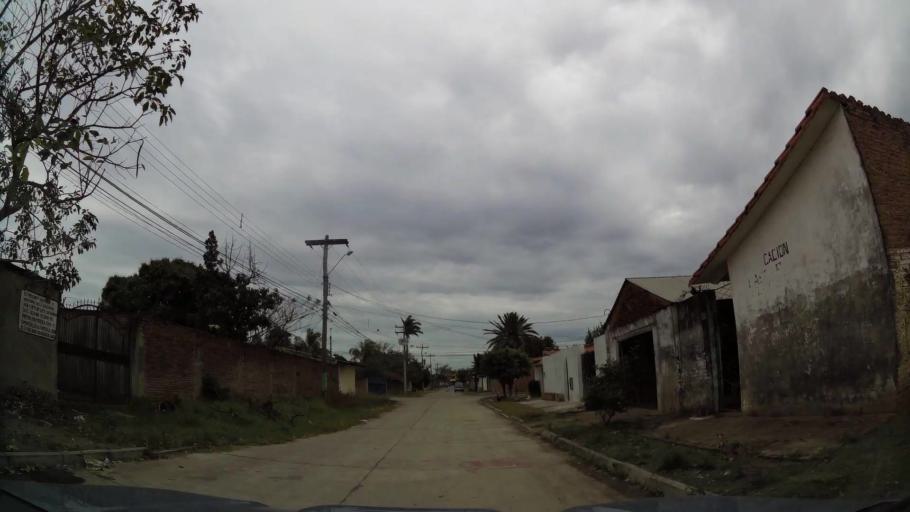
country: BO
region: Santa Cruz
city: Santa Cruz de la Sierra
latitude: -17.7469
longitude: -63.1854
